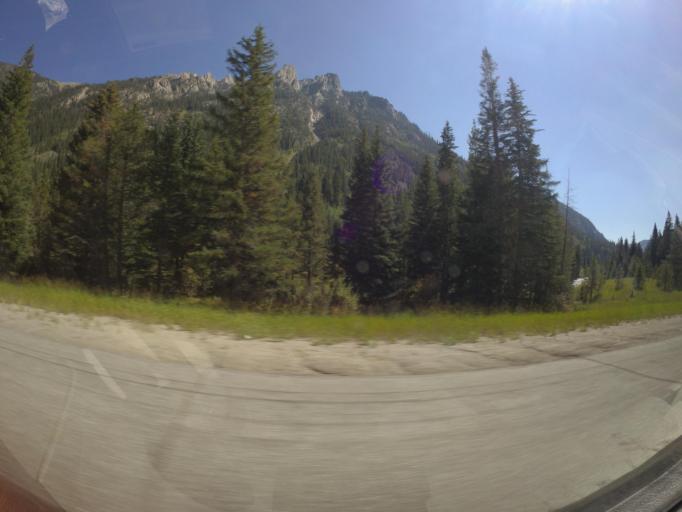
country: US
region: Colorado
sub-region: Summit County
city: Frisco
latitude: 39.5525
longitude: -106.1366
